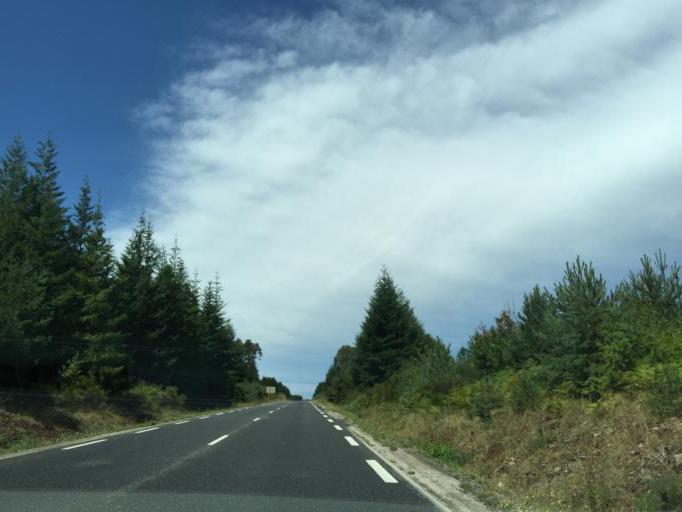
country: FR
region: Midi-Pyrenees
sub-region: Departement de l'Aveyron
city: Millau
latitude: 44.1935
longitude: 3.0227
